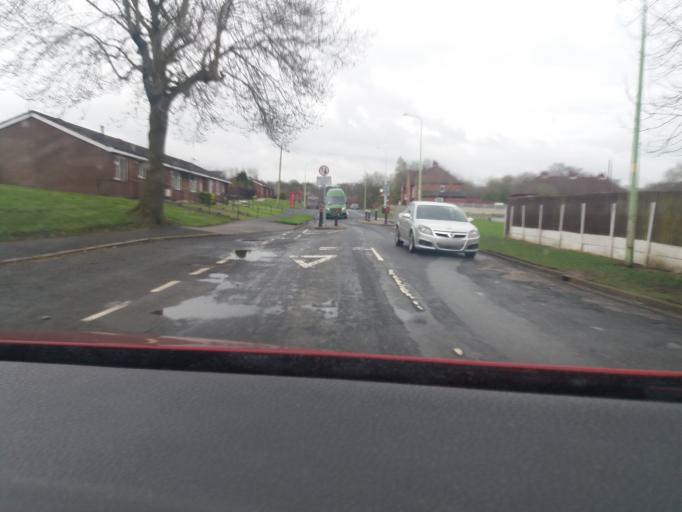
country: GB
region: England
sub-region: Lancashire
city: Coppull
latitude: 53.6392
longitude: -2.6417
